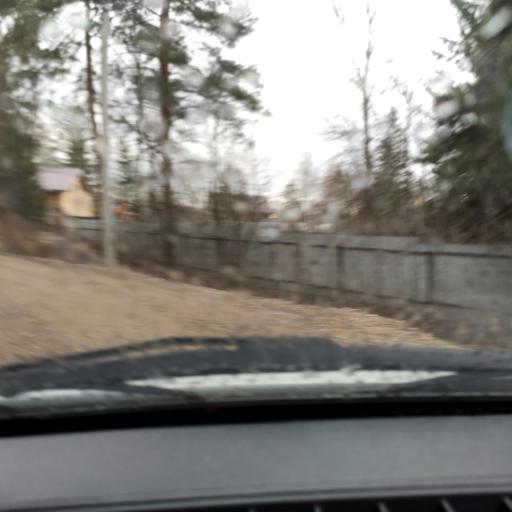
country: RU
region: Bashkortostan
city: Ufa
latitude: 54.7805
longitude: 56.1815
